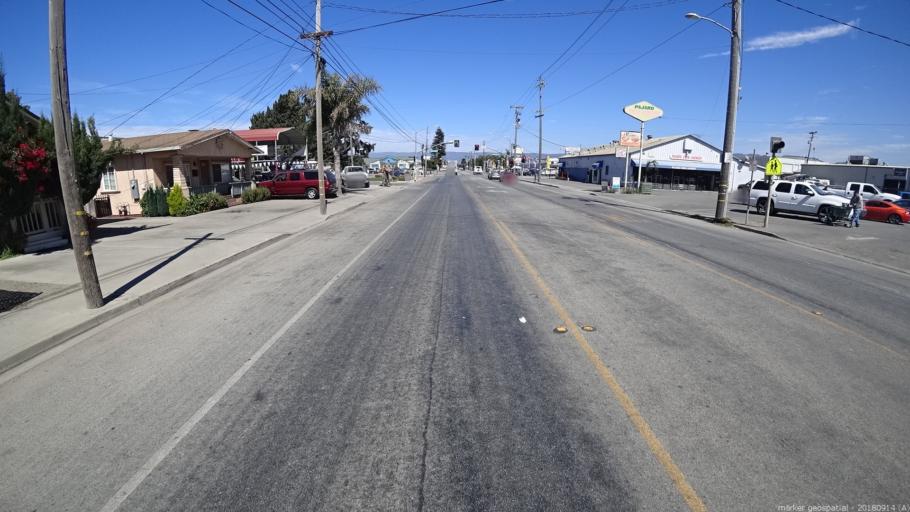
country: US
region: California
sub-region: Monterey County
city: Pajaro
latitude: 36.8982
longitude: -121.7480
